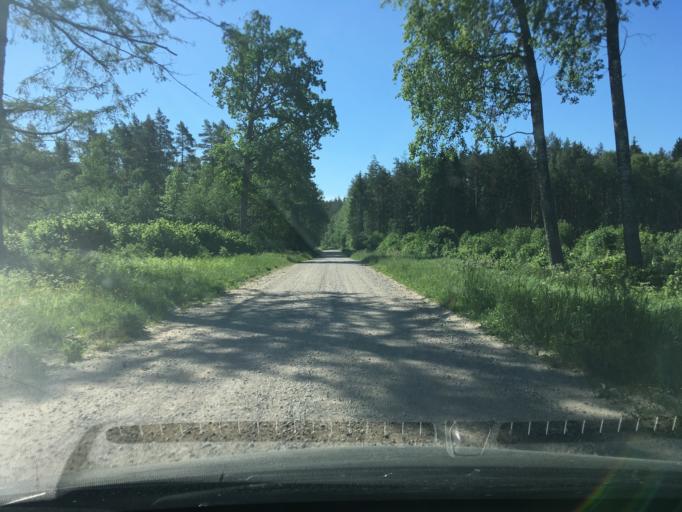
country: EE
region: Laeaene
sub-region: Lihula vald
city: Lihula
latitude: 58.6410
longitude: 23.7898
